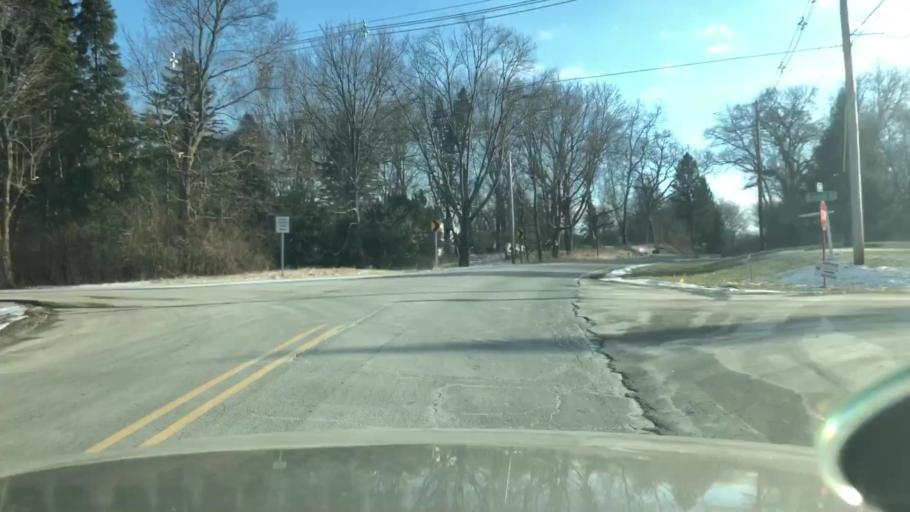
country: US
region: Michigan
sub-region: Jackson County
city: Vandercook Lake
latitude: 42.1603
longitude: -84.4522
